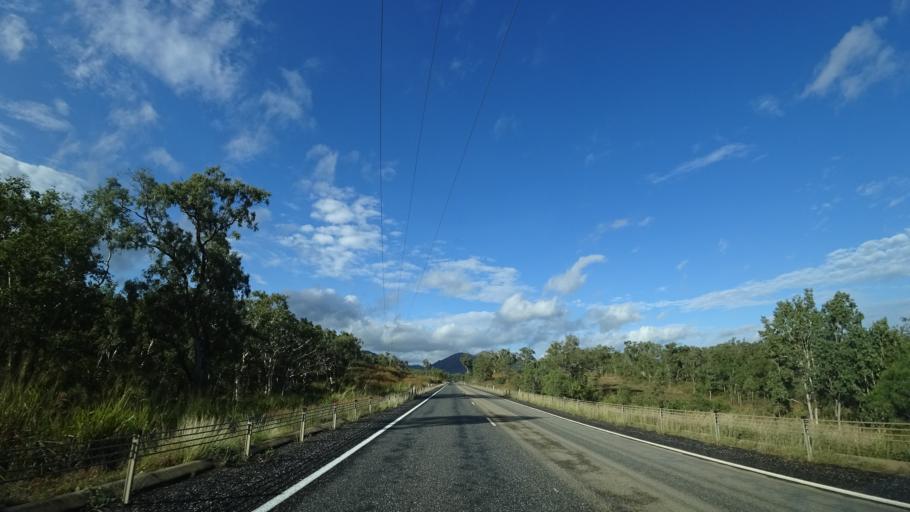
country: AU
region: Queensland
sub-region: Cook
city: Cooktown
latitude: -15.6101
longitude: 145.2215
